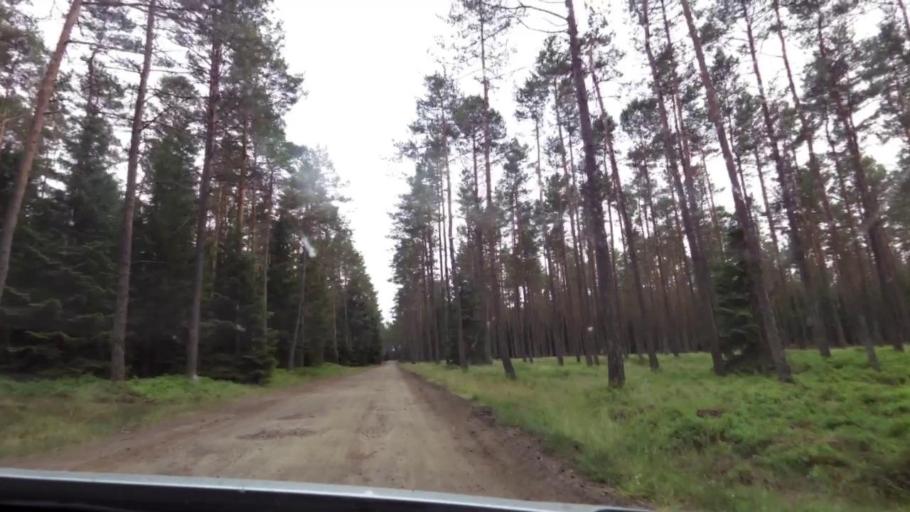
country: PL
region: Pomeranian Voivodeship
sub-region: Powiat bytowski
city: Trzebielino
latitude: 54.2129
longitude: 17.0043
